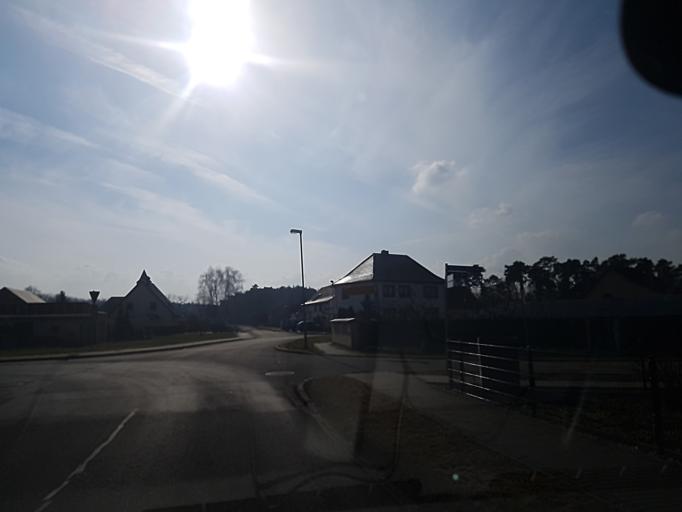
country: DE
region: Brandenburg
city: Wenzlow
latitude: 52.3006
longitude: 12.4453
